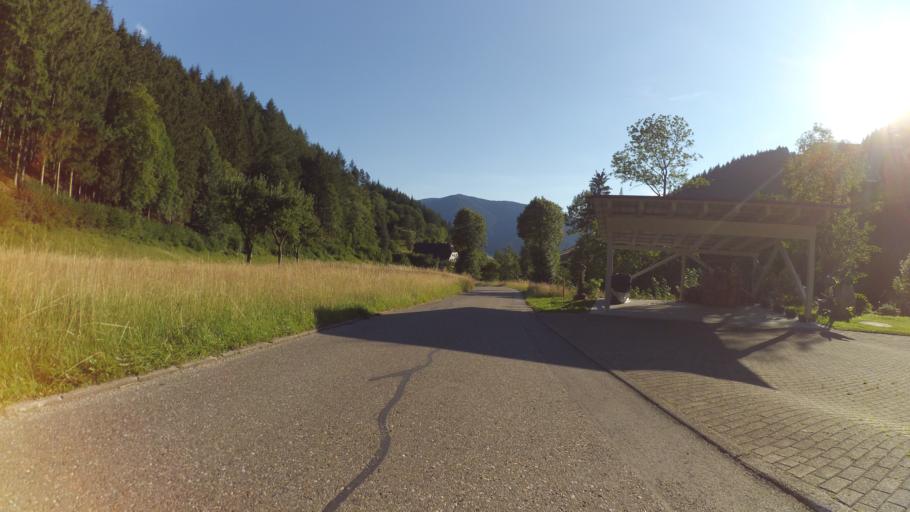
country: DE
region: Baden-Wuerttemberg
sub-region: Freiburg Region
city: Elzach
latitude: 48.1143
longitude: 8.0807
